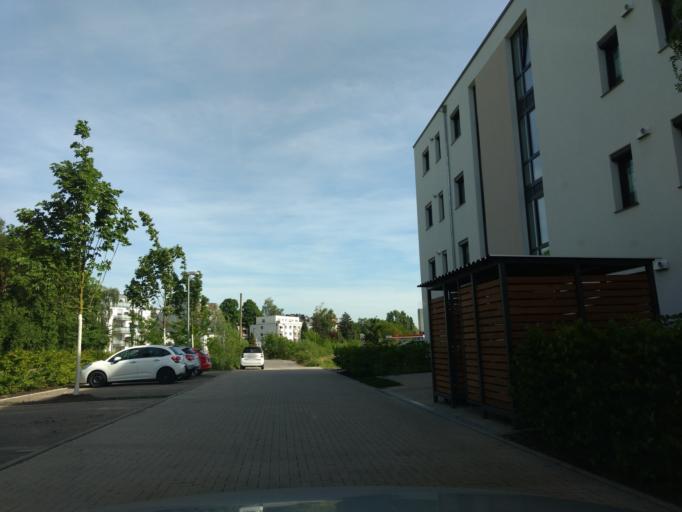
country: DE
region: North Rhine-Westphalia
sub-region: Regierungsbezirk Dusseldorf
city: Erkrath
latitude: 51.2286
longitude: 6.8560
